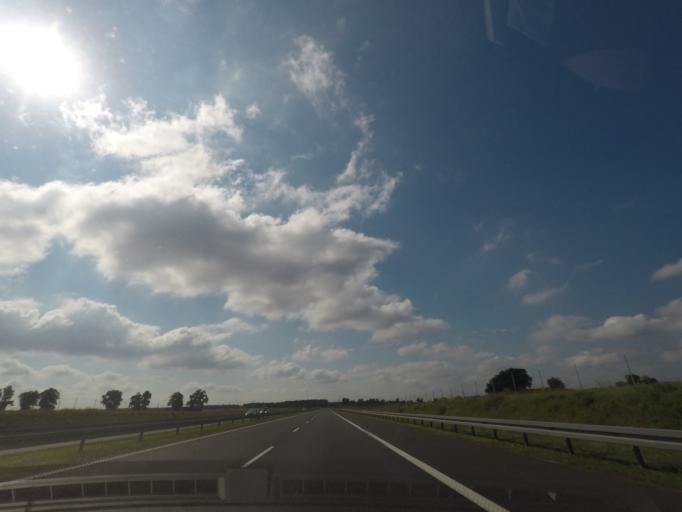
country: PL
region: Kujawsko-Pomorskie
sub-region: Powiat swiecki
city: Warlubie
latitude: 53.5618
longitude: 18.6097
